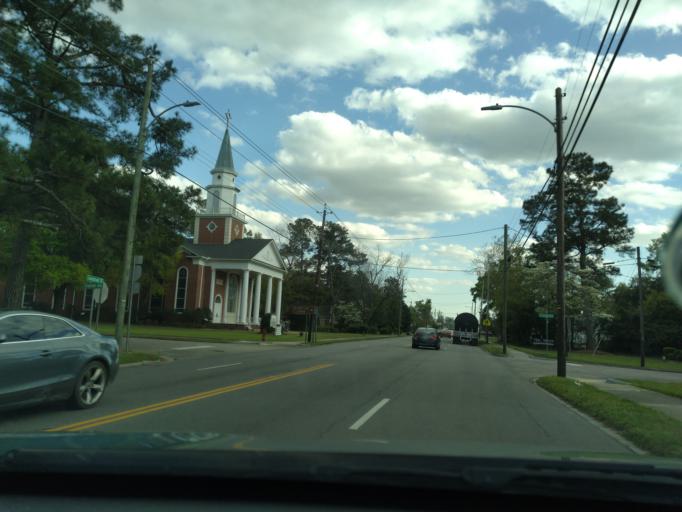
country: US
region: South Carolina
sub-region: Williamsburg County
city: Kingstree
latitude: 33.6704
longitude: -79.8359
